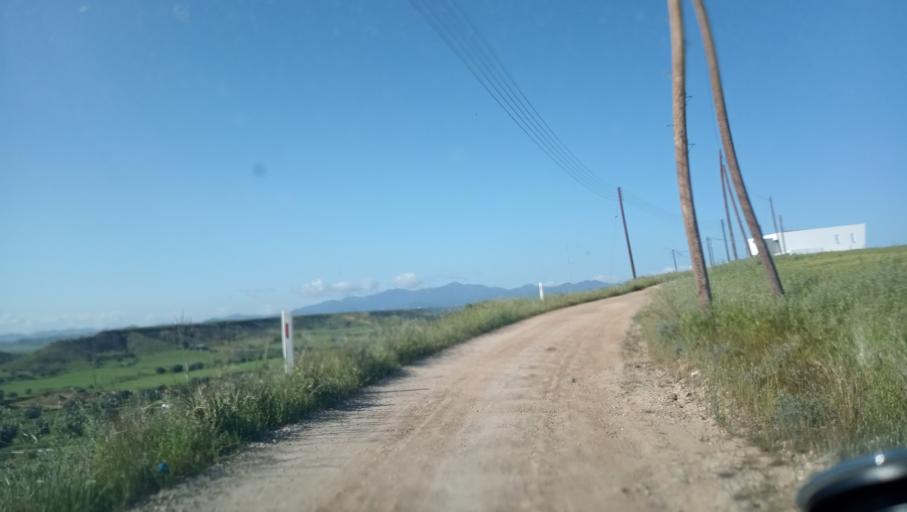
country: CY
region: Lefkosia
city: Tseri
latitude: 35.0688
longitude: 33.3144
